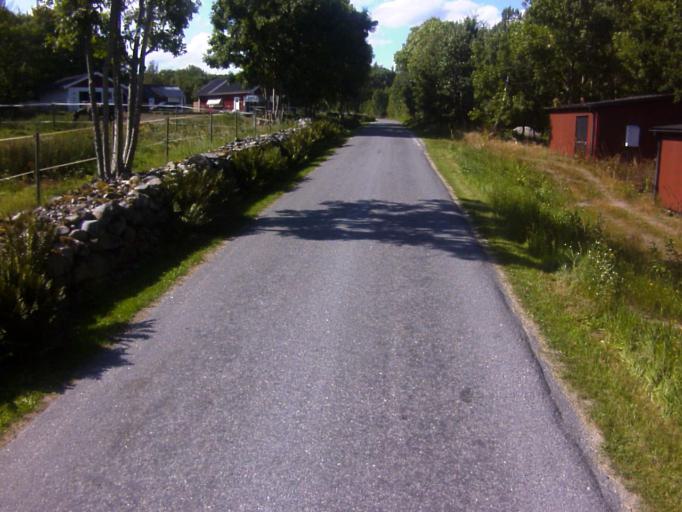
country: SE
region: Blekinge
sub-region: Solvesborgs Kommun
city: Soelvesborg
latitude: 56.1054
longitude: 14.6153
